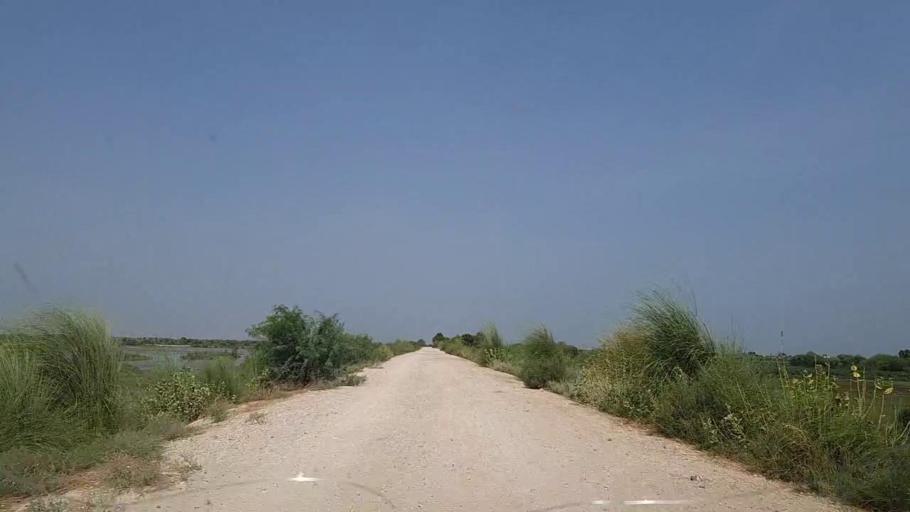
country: PK
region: Sindh
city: Ghotki
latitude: 28.1179
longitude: 69.3710
